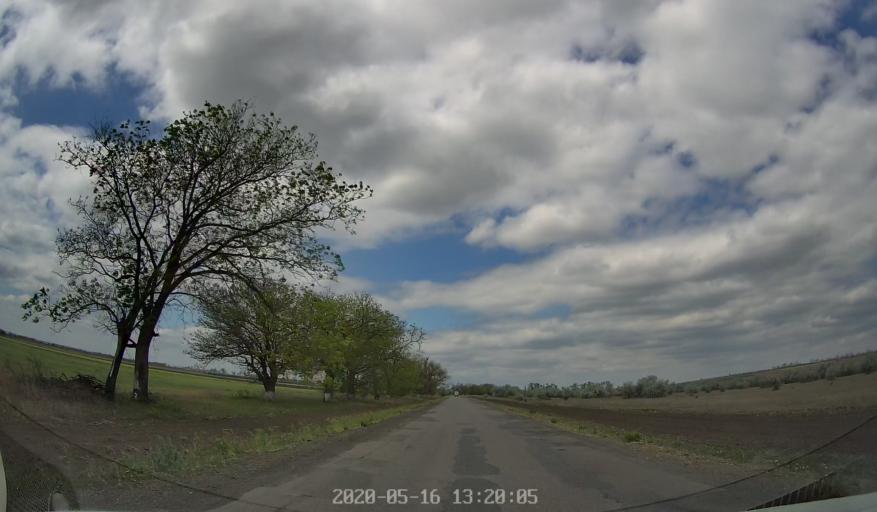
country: UA
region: Odessa
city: Lymanske
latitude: 46.5377
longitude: 30.0528
